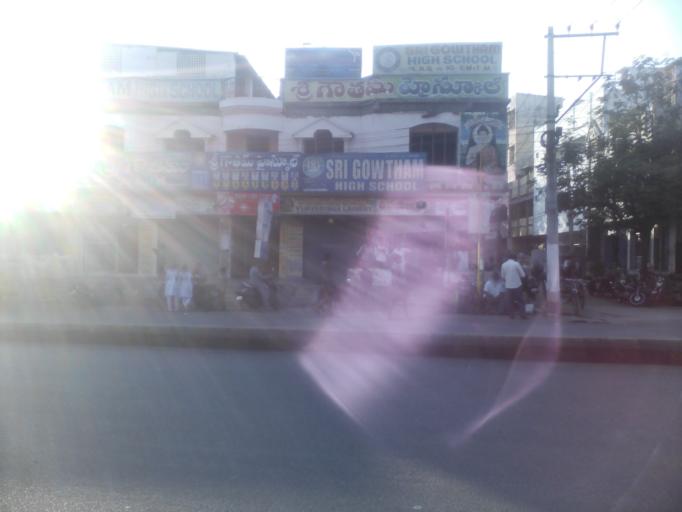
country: IN
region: Andhra Pradesh
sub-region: Krishna
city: Vijayawada
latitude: 16.5305
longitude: 80.6123
